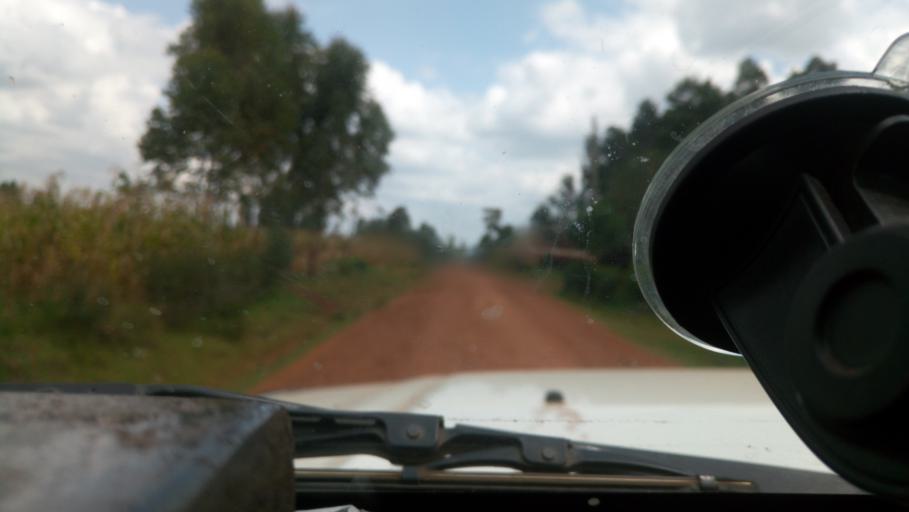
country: KE
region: Kisii
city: Ogembo
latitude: -0.7607
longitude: 34.7337
